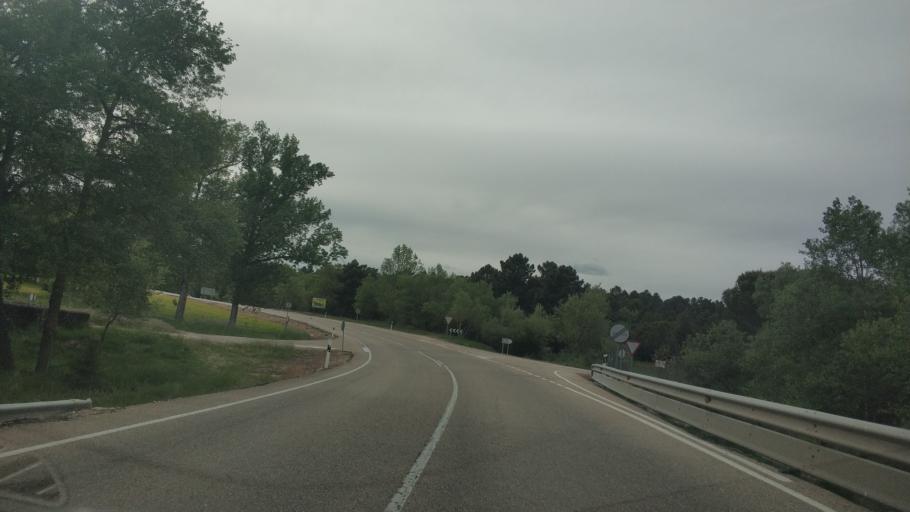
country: ES
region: Castille and Leon
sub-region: Provincia de Soria
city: Bayubas de Abajo
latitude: 41.5036
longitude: -2.8891
